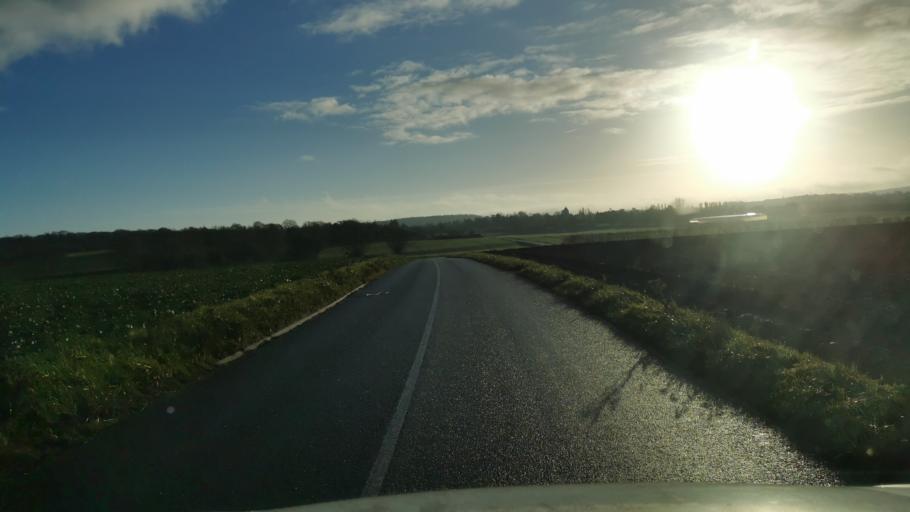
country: FR
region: Ile-de-France
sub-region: Departement des Yvelines
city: Bazainville
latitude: 48.8095
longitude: 1.6561
